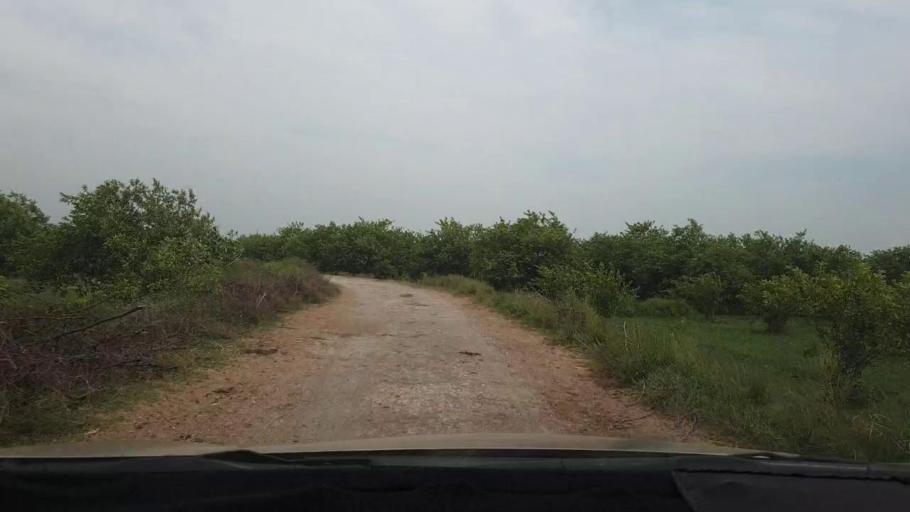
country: PK
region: Sindh
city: Naudero
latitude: 27.6336
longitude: 68.3435
